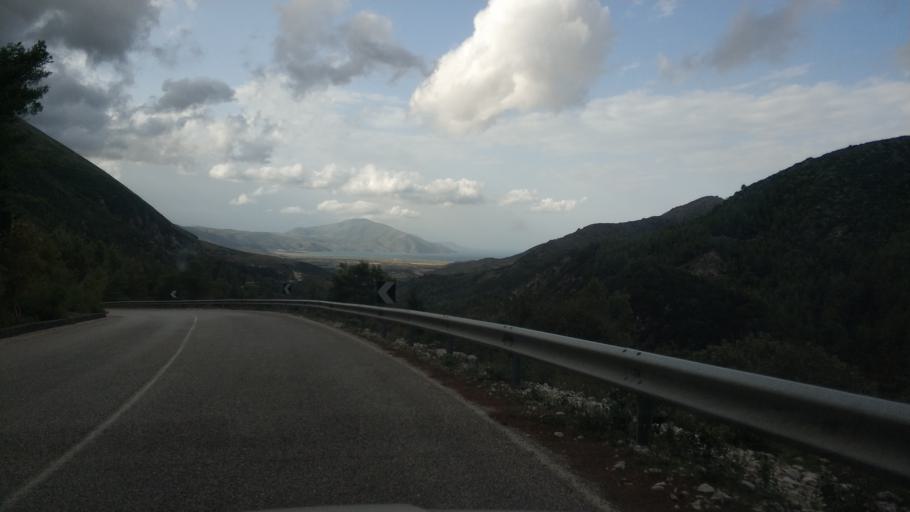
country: AL
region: Vlore
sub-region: Rrethi i Vlores
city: Orikum
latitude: 40.2536
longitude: 19.5366
